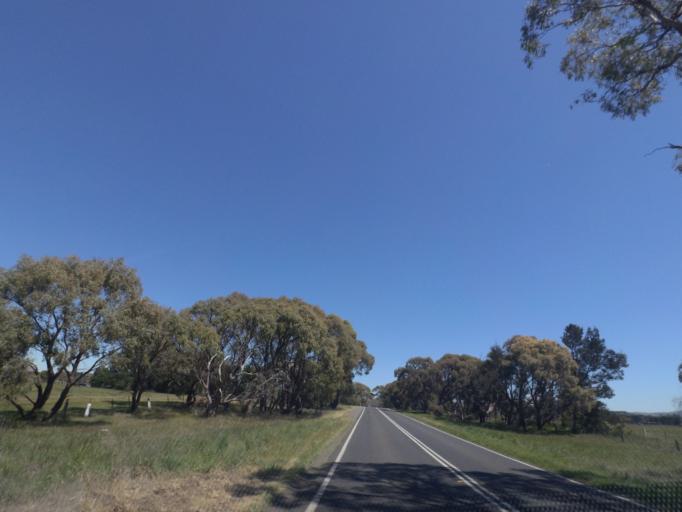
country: AU
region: Victoria
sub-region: Whittlesea
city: Whittlesea
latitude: -37.2929
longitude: 144.9232
